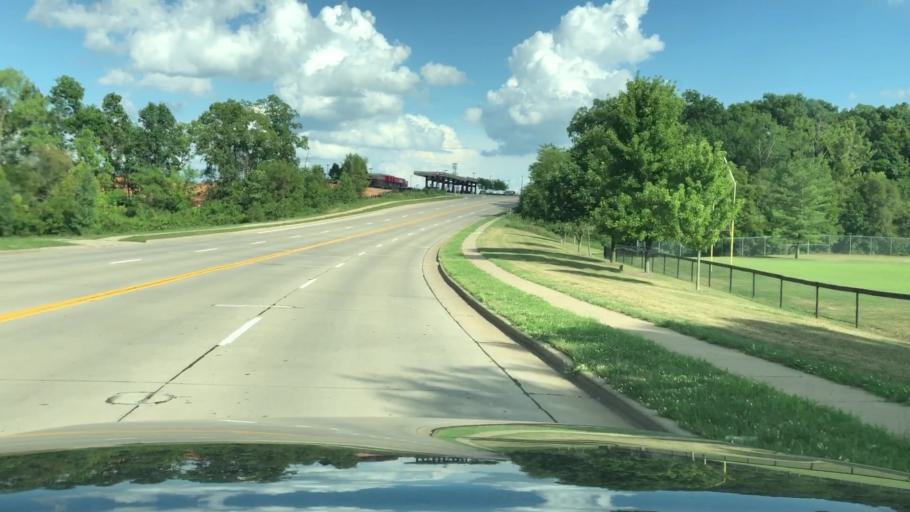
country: US
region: Missouri
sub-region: Saint Charles County
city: Wentzville
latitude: 38.8244
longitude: -90.8559
